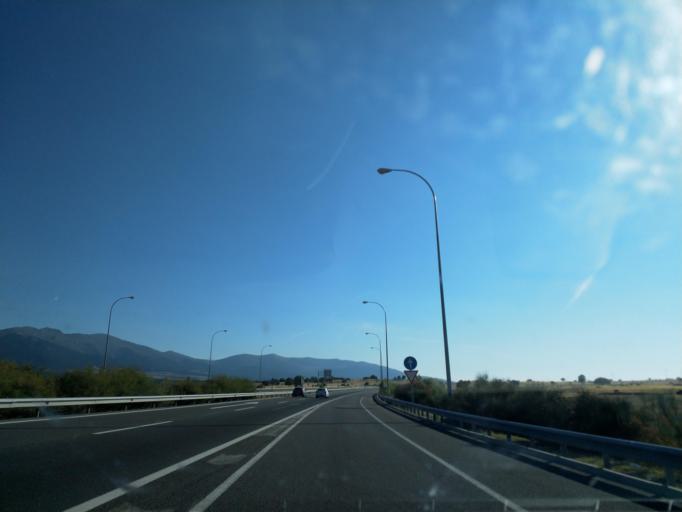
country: ES
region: Castille and Leon
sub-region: Provincia de Segovia
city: Segovia
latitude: 40.9016
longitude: -4.1050
